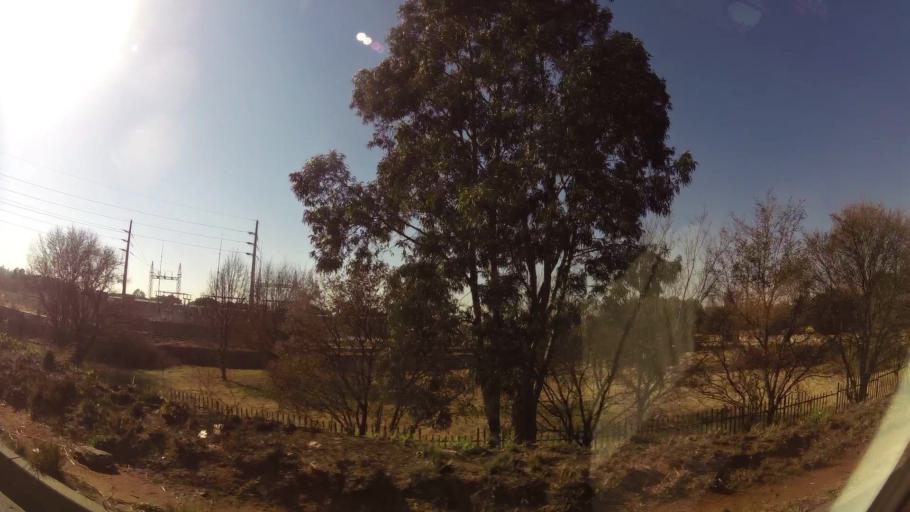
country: ZA
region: Gauteng
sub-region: Ekurhuleni Metropolitan Municipality
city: Germiston
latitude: -26.2229
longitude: 28.1152
